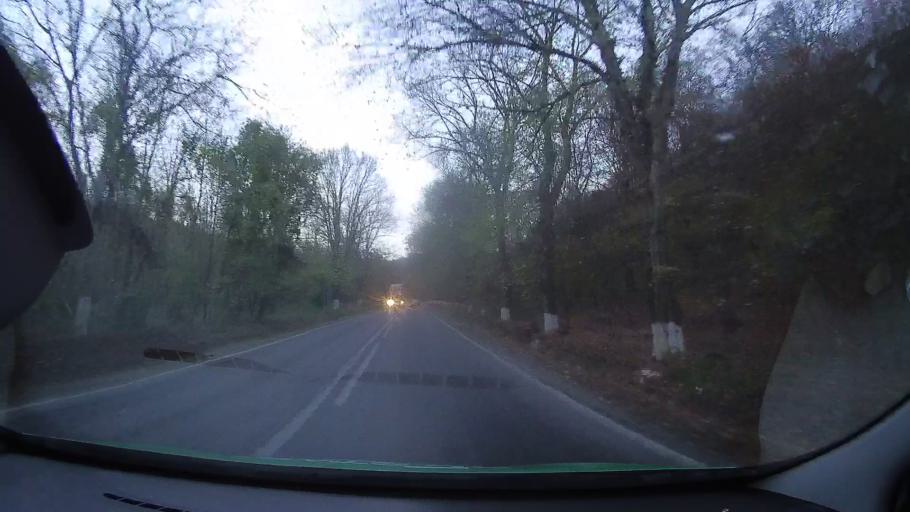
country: RO
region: Constanta
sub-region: Comuna Lipnita
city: Lipnita
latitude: 44.0959
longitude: 27.6501
